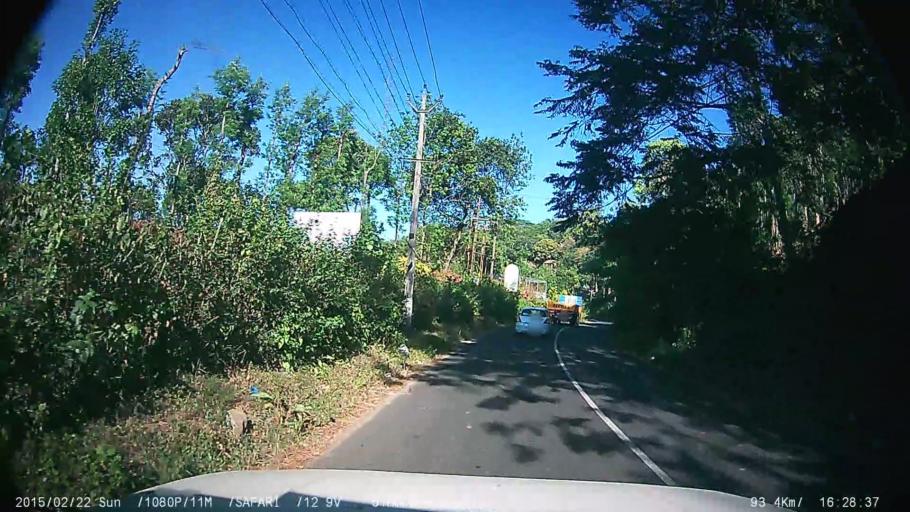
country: IN
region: Tamil Nadu
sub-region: Theni
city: Gudalur
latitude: 9.6113
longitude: 77.1482
